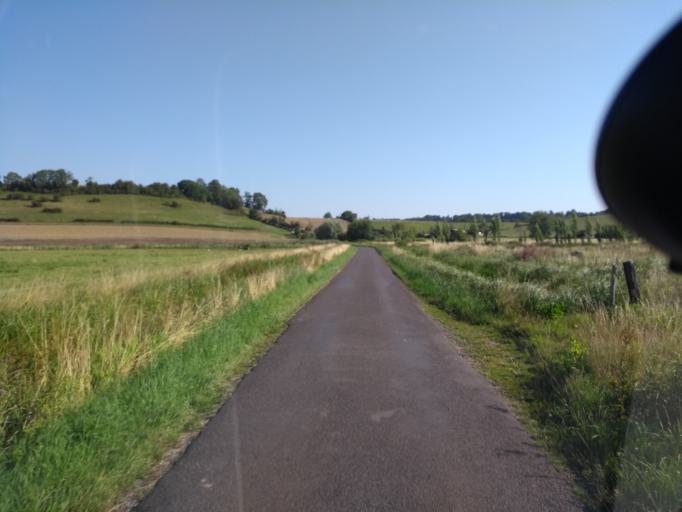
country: GB
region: England
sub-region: Somerset
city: Westonzoyland
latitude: 51.1355
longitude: -2.9164
